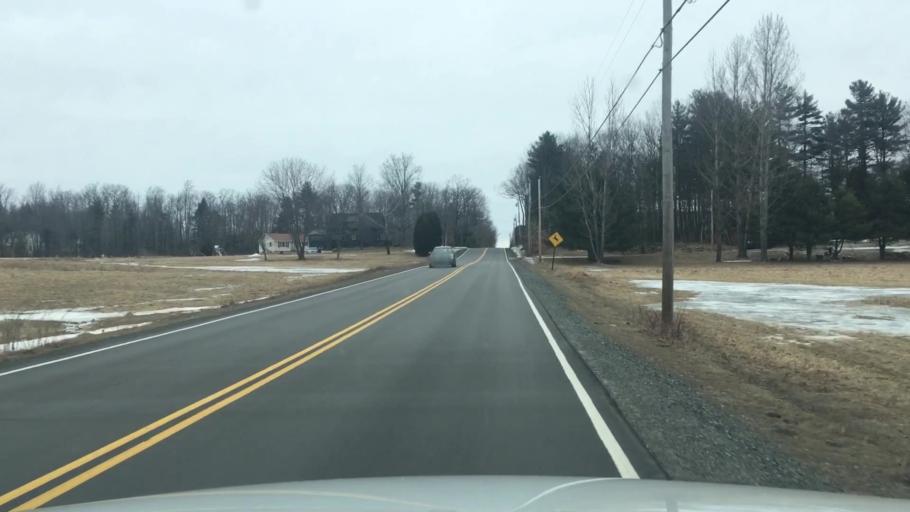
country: US
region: Maine
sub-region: York County
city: Springvale
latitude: 43.4466
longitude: -70.8153
